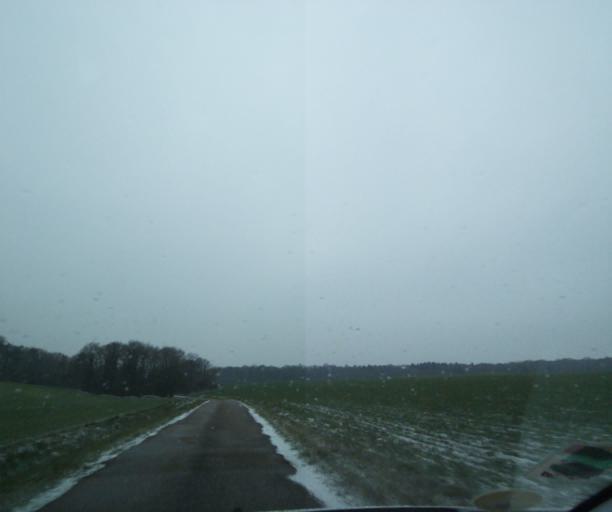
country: FR
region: Champagne-Ardenne
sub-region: Departement de la Haute-Marne
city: Wassy
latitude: 48.4639
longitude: 5.0195
